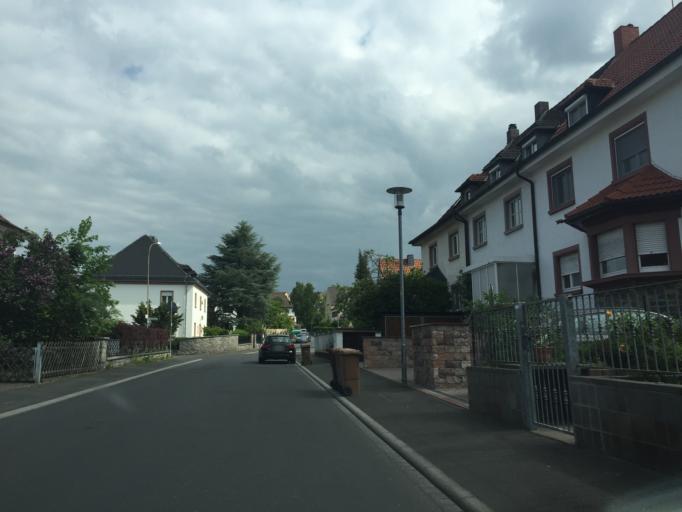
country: DE
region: Bavaria
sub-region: Regierungsbezirk Unterfranken
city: Aschaffenburg
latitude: 49.9729
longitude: 9.1689
